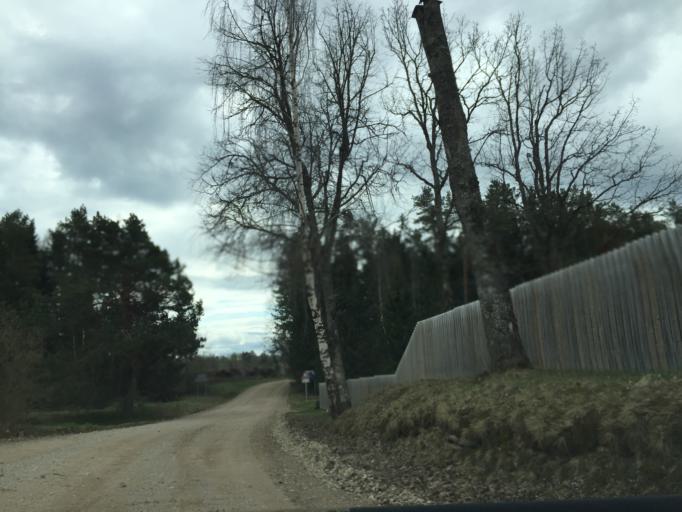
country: LV
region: Jaunpiebalga
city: Jaunpiebalga
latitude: 57.1672
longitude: 26.0699
